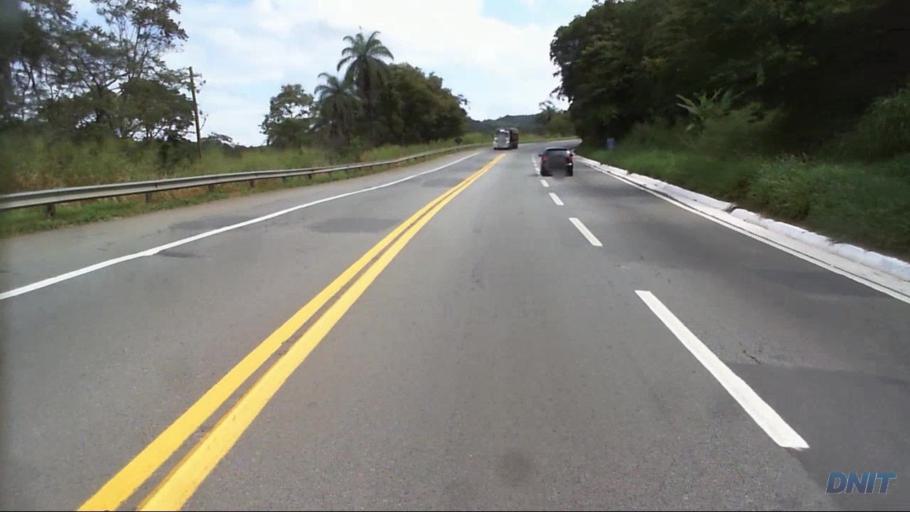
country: BR
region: Minas Gerais
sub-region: Santa Luzia
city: Santa Luzia
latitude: -19.8003
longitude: -43.7500
